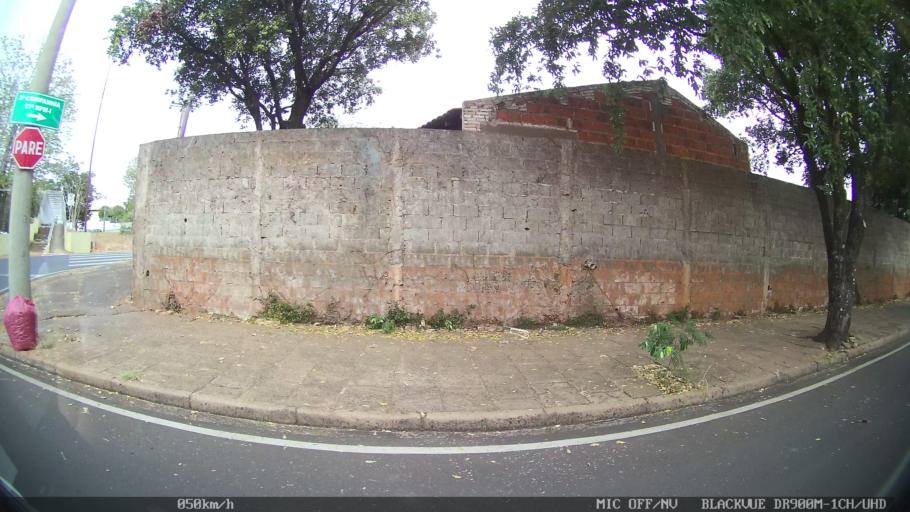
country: BR
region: Sao Paulo
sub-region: Sao Jose Do Rio Preto
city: Sao Jose do Rio Preto
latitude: -20.8235
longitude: -49.3700
